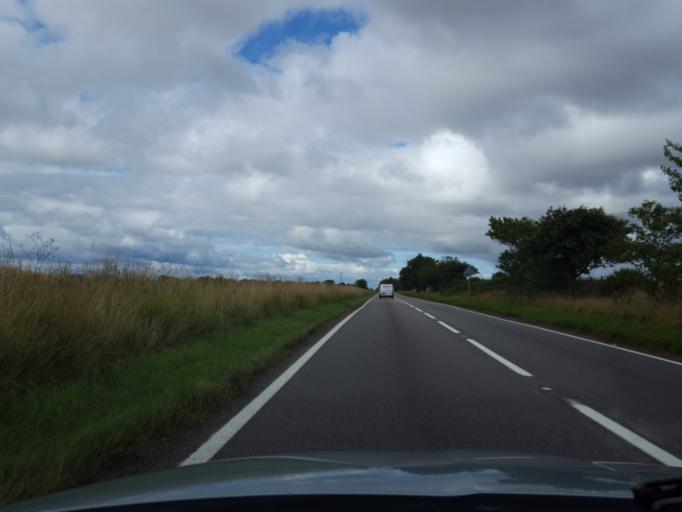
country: GB
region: Scotland
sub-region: Moray
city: Kinloss
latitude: 57.6258
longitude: -3.5227
